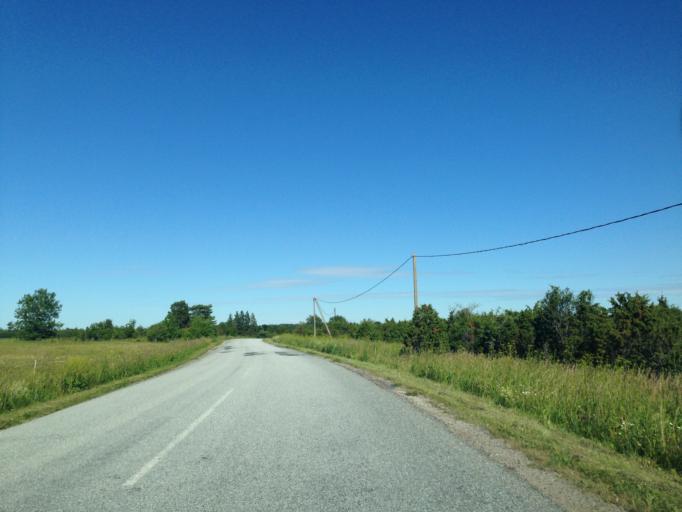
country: EE
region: Harju
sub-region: Raasiku vald
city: Raasiku
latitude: 59.4578
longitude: 25.2135
